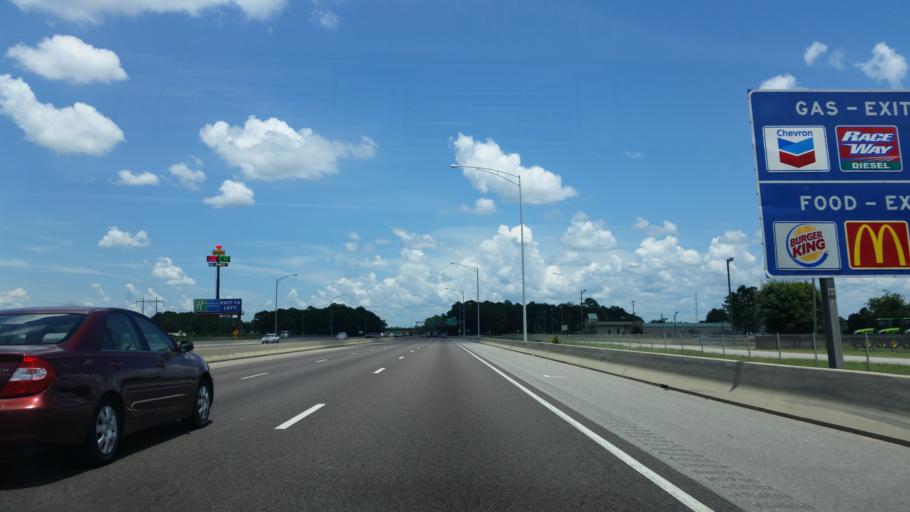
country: US
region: Alabama
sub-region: Mobile County
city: Prichard
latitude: 30.7365
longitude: -88.1136
